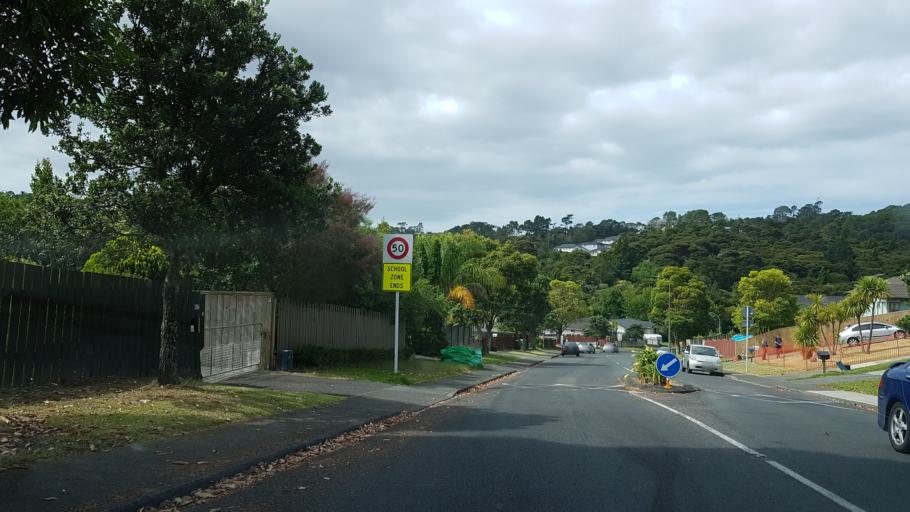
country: NZ
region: Auckland
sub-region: Auckland
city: North Shore
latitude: -36.7723
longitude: 174.7083
